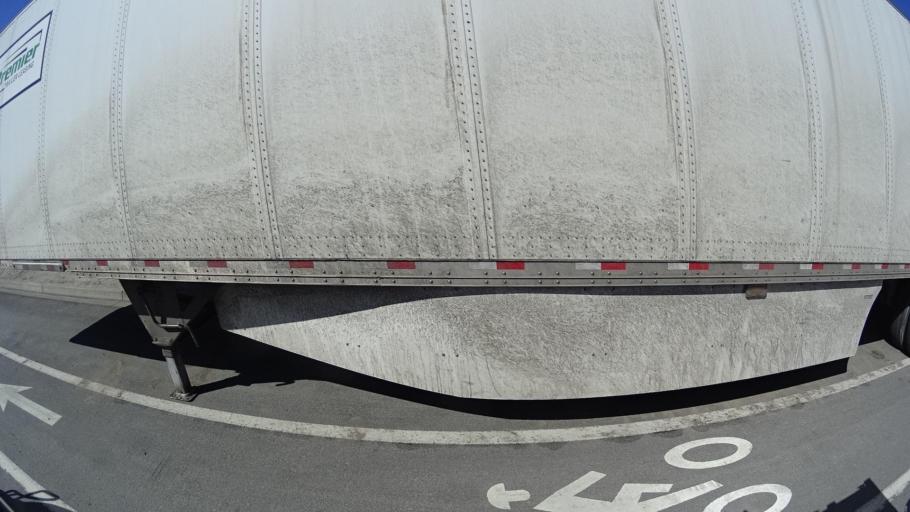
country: US
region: Nevada
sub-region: Washoe County
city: Lemmon Valley
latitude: 39.6460
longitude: -119.8970
